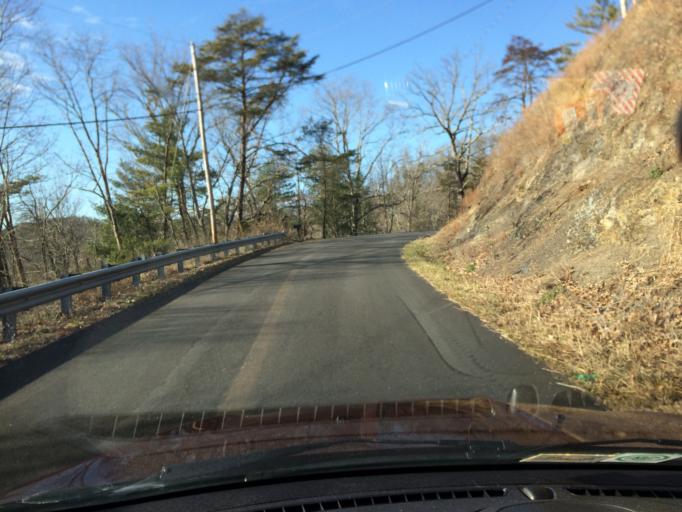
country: US
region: Virginia
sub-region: Alleghany County
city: Clifton Forge
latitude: 37.7055
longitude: -79.8235
